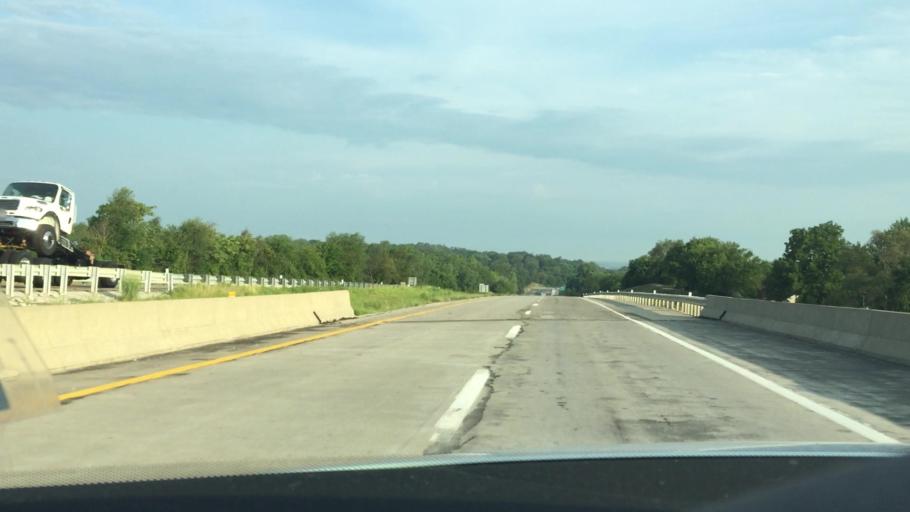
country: US
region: Missouri
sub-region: Buchanan County
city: Saint Joseph
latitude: 39.7220
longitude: -94.8341
